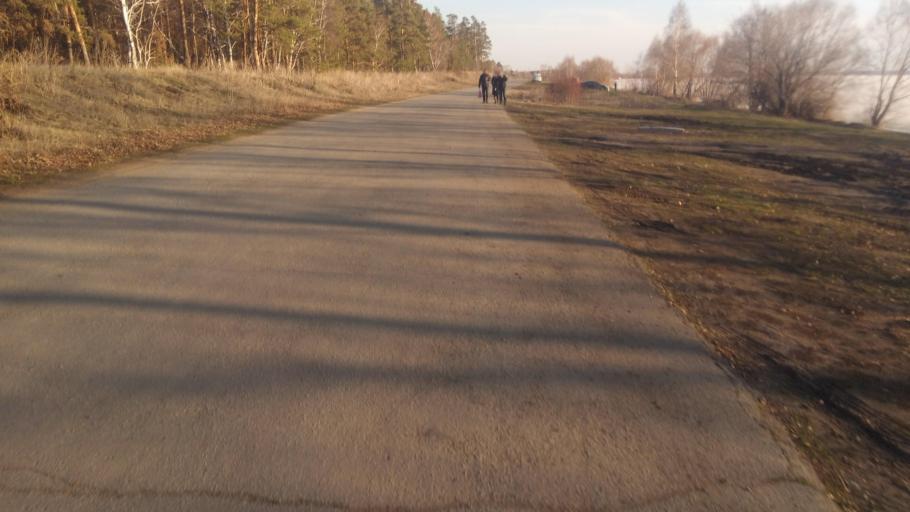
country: RU
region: Chelyabinsk
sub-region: Gorod Chelyabinsk
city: Chelyabinsk
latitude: 55.1310
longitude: 61.3281
